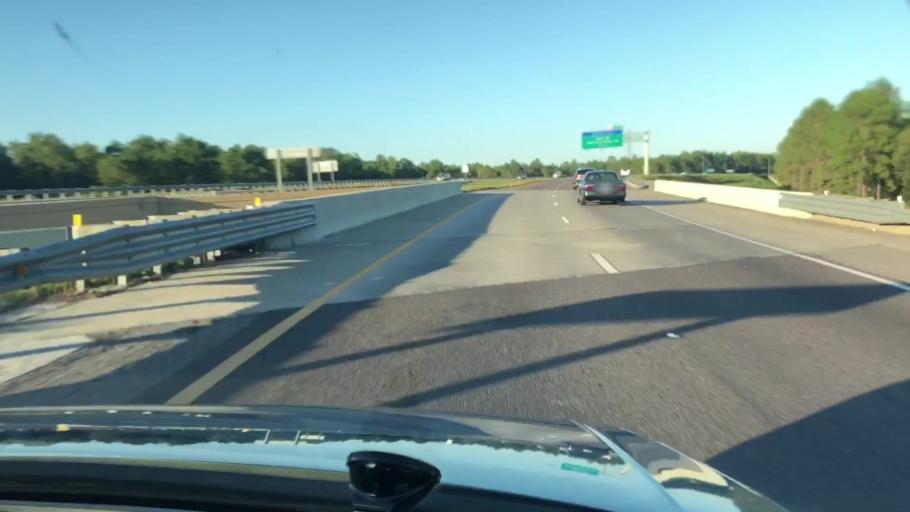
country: US
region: Florida
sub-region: Orange County
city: Ocoee
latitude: 28.5948
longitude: -81.5565
